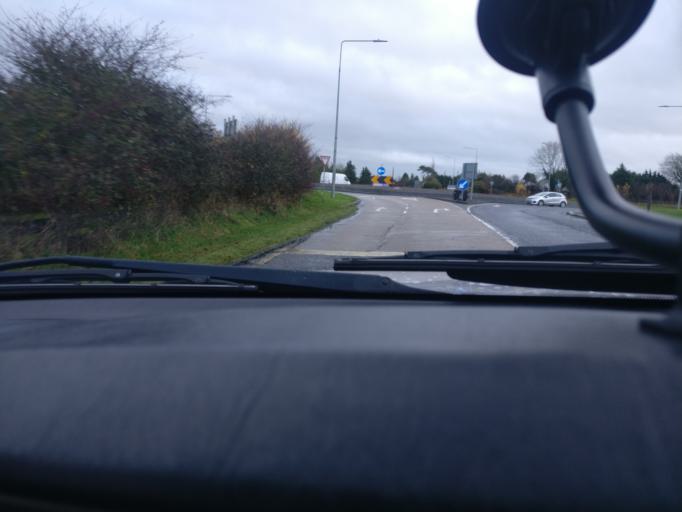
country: IE
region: Leinster
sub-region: An Mhi
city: Enfield
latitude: 53.4132
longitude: -6.8171
